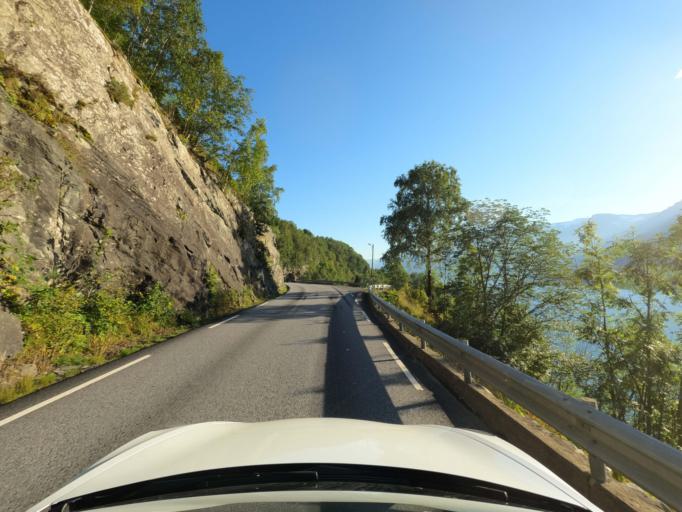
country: NO
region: Hordaland
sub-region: Ullensvang
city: Kinsarvik
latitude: 60.2856
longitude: 6.6235
